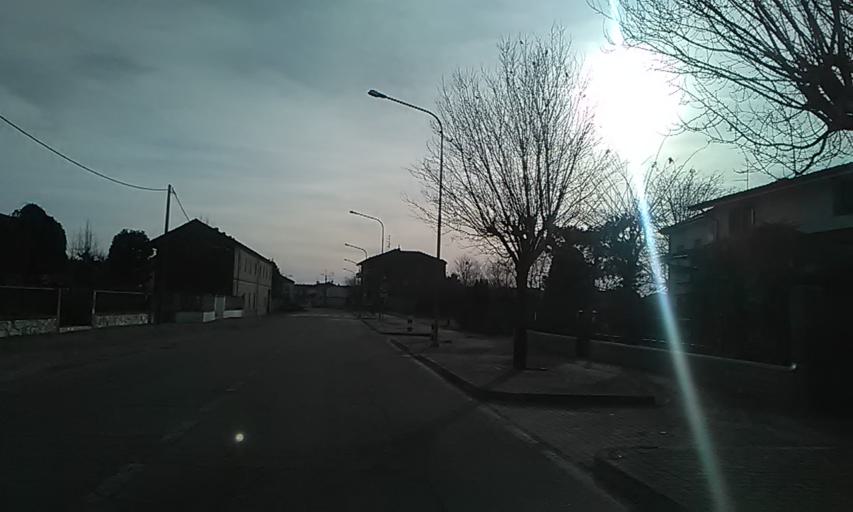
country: IT
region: Piedmont
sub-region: Provincia di Vercelli
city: Stroppiana
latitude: 45.2353
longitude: 8.4560
